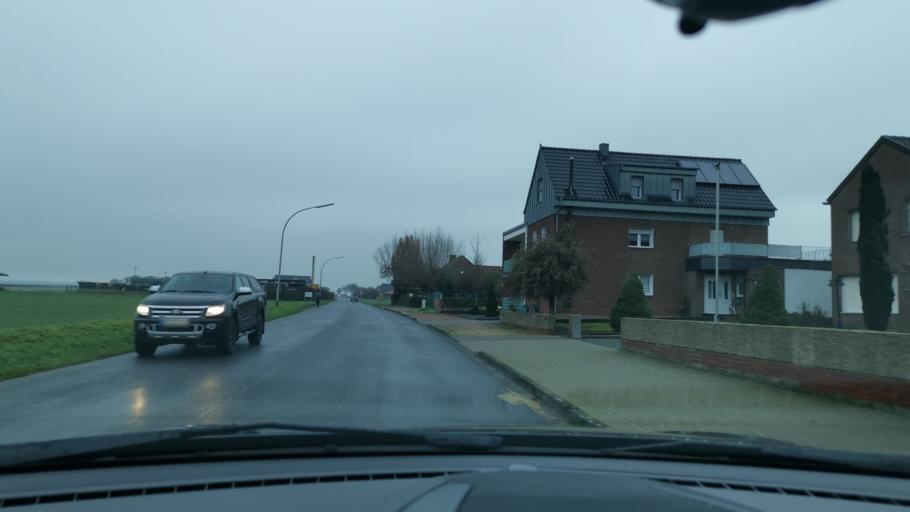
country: DE
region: North Rhine-Westphalia
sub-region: Regierungsbezirk Dusseldorf
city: Juchen
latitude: 51.1157
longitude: 6.5407
